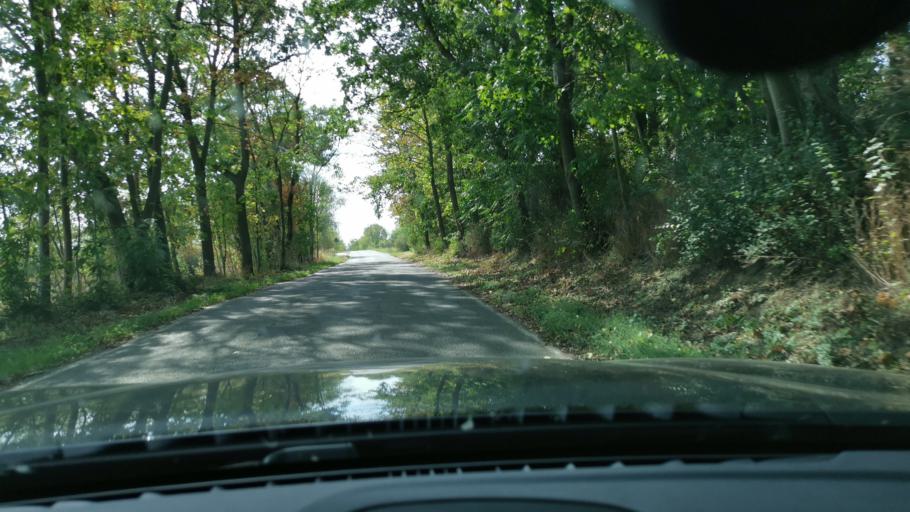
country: DE
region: Saxony
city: Hohburg
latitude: 51.4385
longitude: 12.7550
